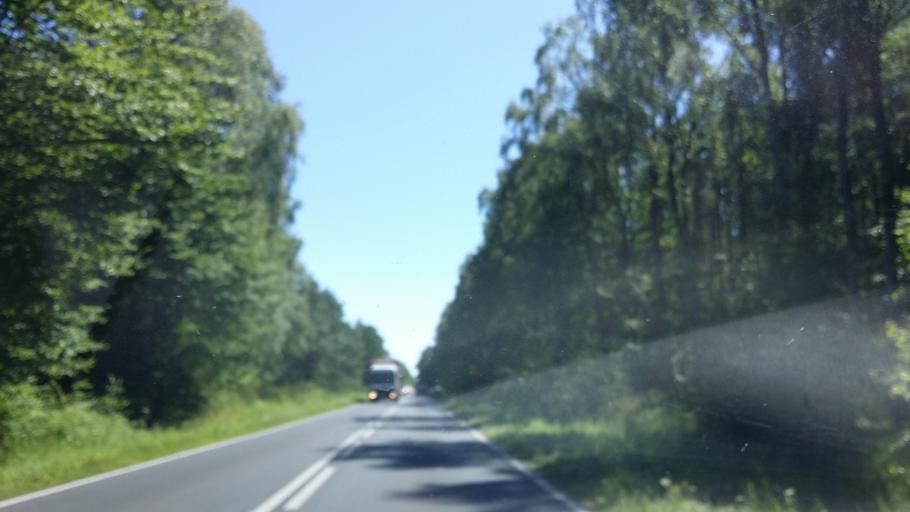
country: PL
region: West Pomeranian Voivodeship
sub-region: Powiat kolobrzeski
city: Kolobrzeg
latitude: 54.1200
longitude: 15.5847
